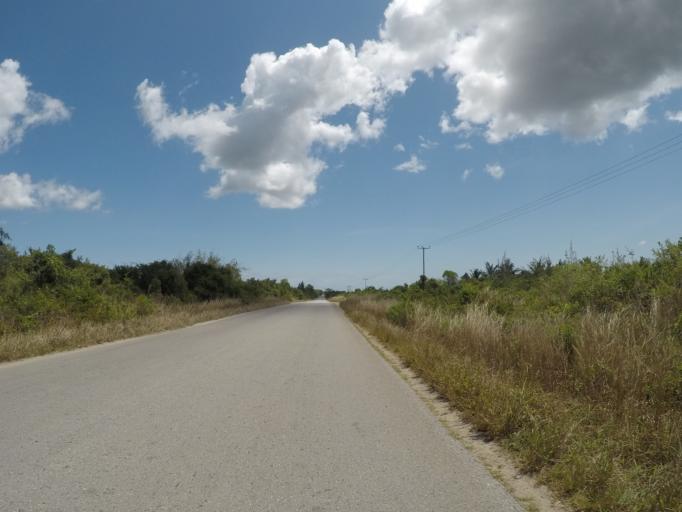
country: TZ
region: Zanzibar Central/South
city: Nganane
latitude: -6.2770
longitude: 39.4837
